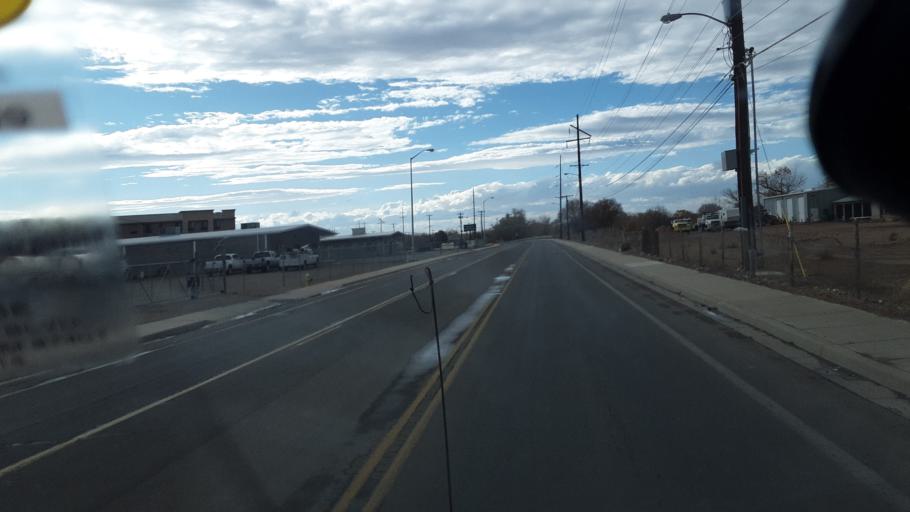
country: US
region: New Mexico
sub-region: San Juan County
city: Farmington
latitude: 36.7267
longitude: -108.1862
